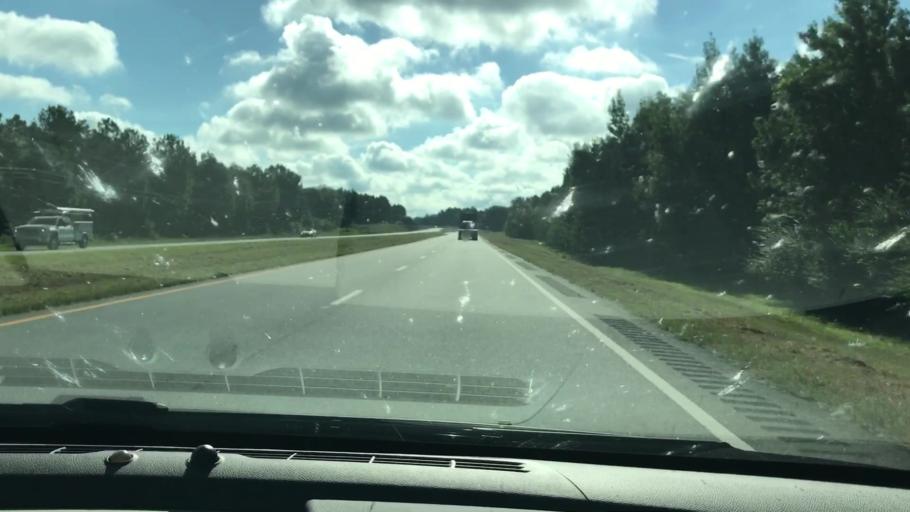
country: US
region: Georgia
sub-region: Worth County
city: Sylvester
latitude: 31.5518
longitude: -83.9751
